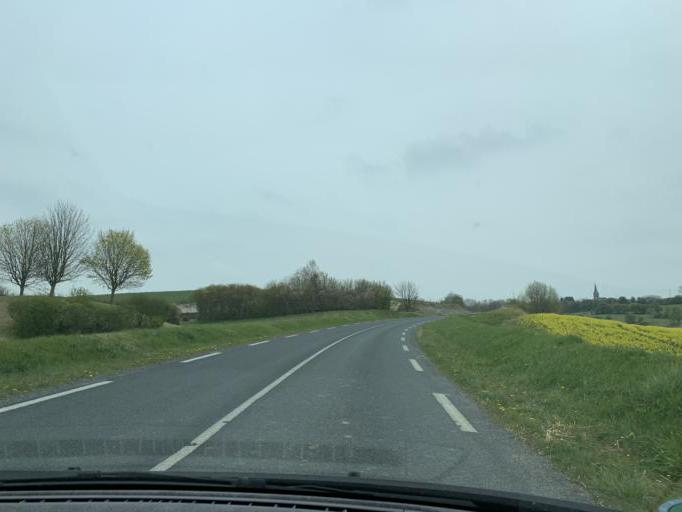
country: FR
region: Haute-Normandie
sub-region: Departement de la Seine-Maritime
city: Londinieres
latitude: 49.8432
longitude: 1.4595
